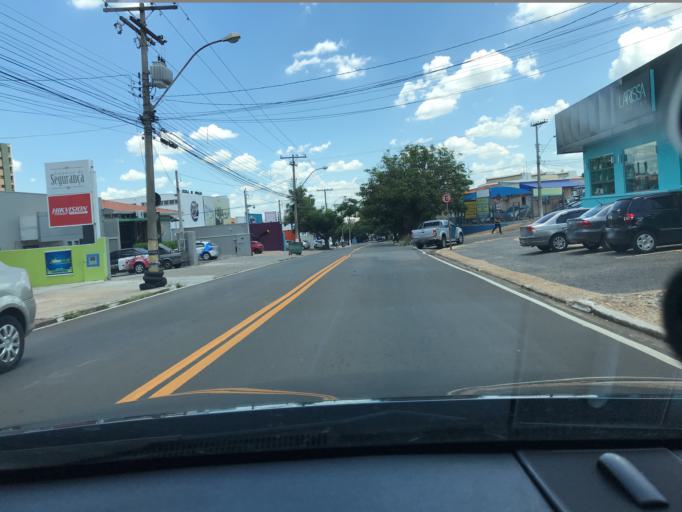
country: BR
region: Sao Paulo
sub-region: Campinas
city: Campinas
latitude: -22.8821
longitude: -47.0720
